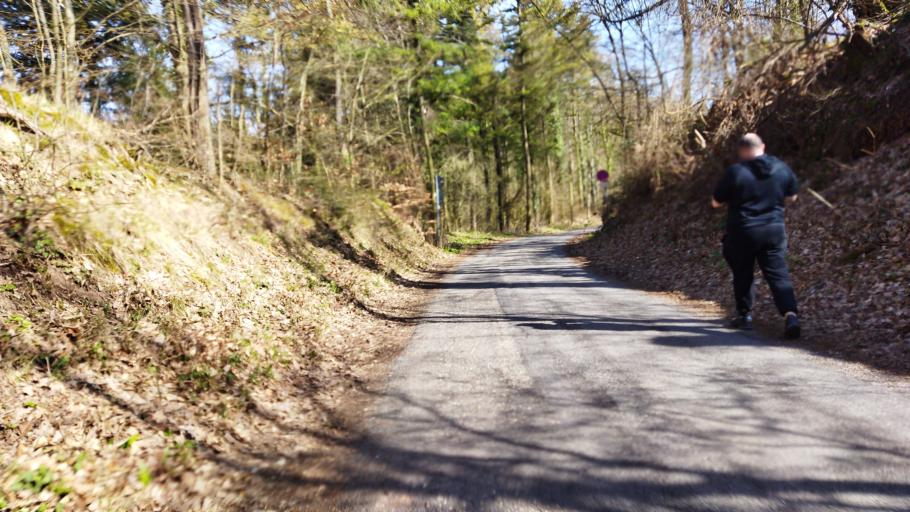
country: DE
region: Baden-Wuerttemberg
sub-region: Regierungsbezirk Stuttgart
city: Eppingen
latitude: 49.1160
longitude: 8.9333
